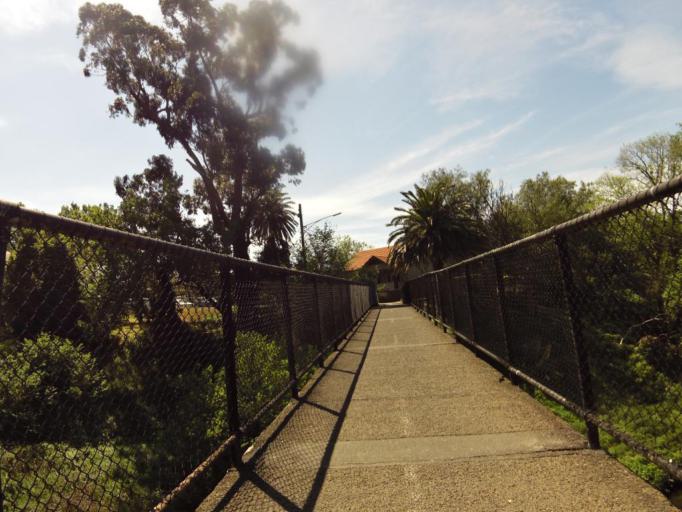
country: AU
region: Victoria
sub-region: Yarra
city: Clifton Hill
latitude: -37.7830
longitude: 144.9930
